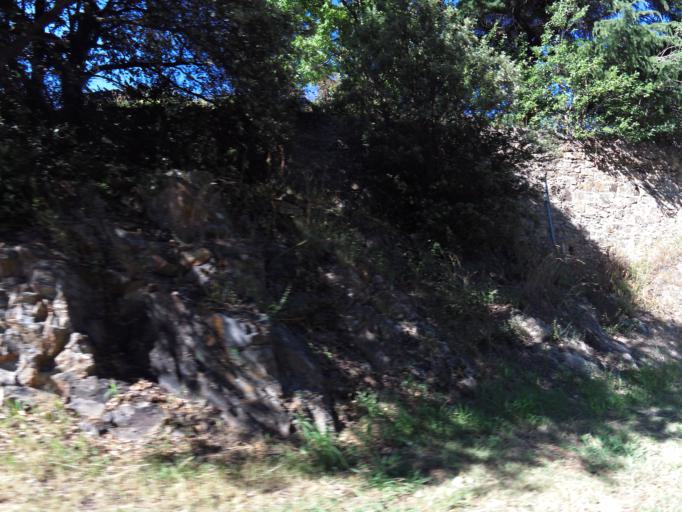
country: FR
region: Languedoc-Roussillon
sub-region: Departement du Gard
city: Saint-Jean-du-Gard
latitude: 44.1126
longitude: 3.8593
